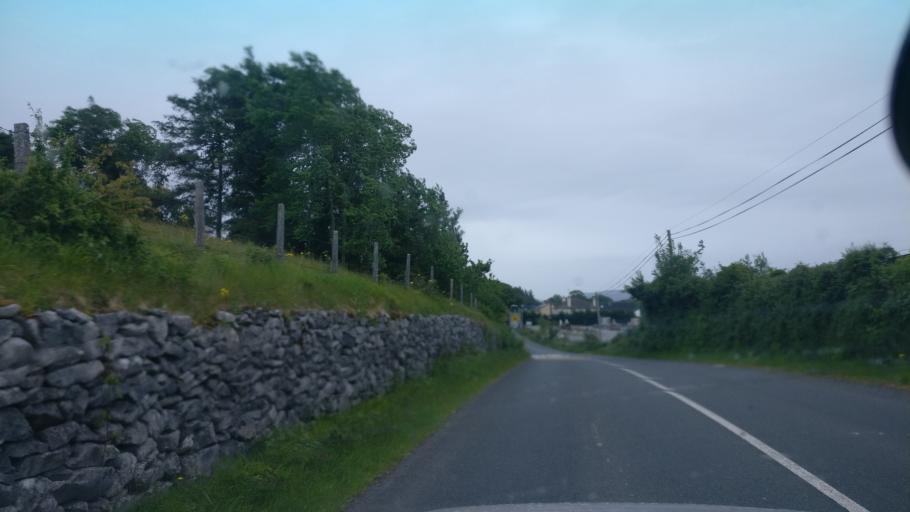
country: IE
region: Connaught
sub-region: County Galway
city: Gort
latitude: 53.0710
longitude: -8.7848
